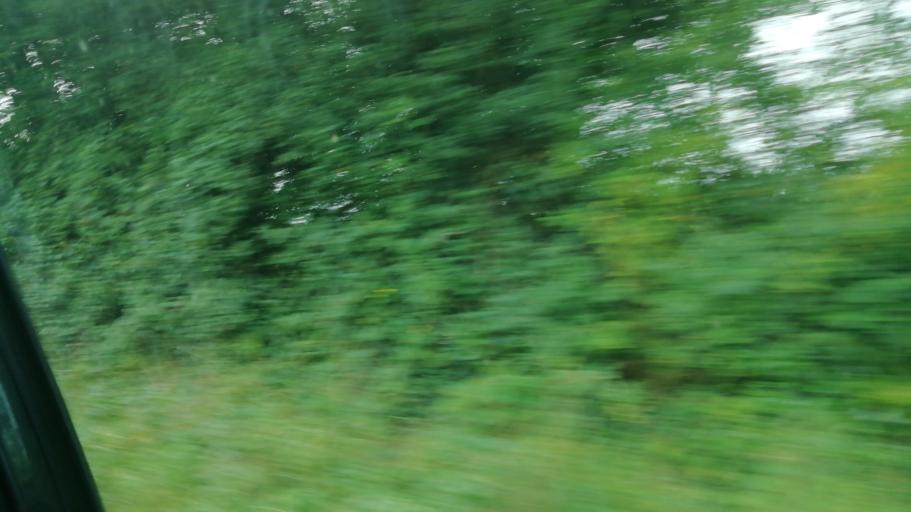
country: IE
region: Leinster
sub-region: Kilkenny
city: Callan
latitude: 52.5507
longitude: -7.5394
